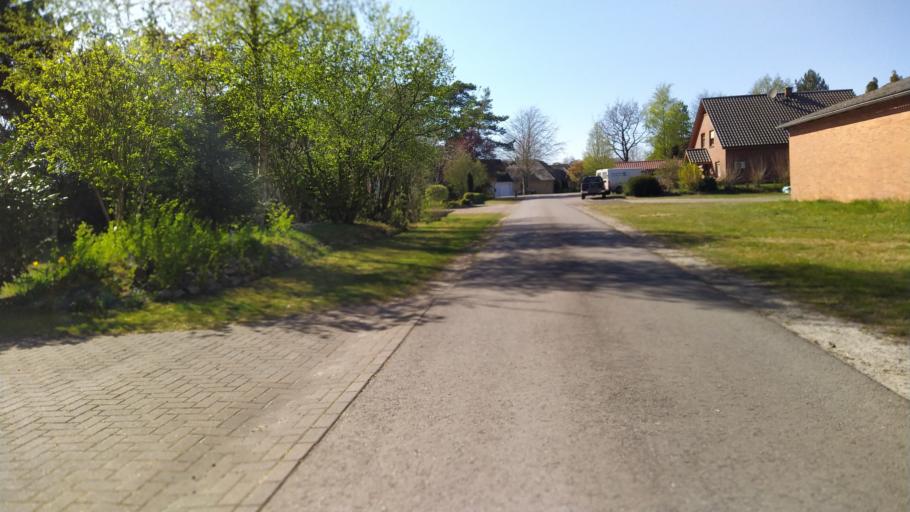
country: DE
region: Lower Saxony
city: Heeslingen
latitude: 53.3321
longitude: 9.3826
